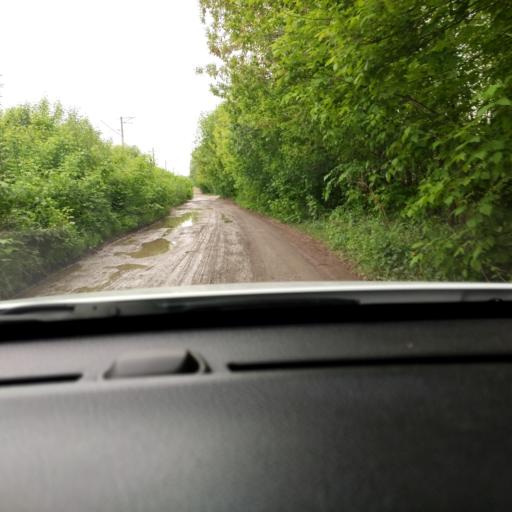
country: RU
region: Tatarstan
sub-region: Gorod Kazan'
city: Kazan
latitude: 55.8464
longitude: 49.1731
